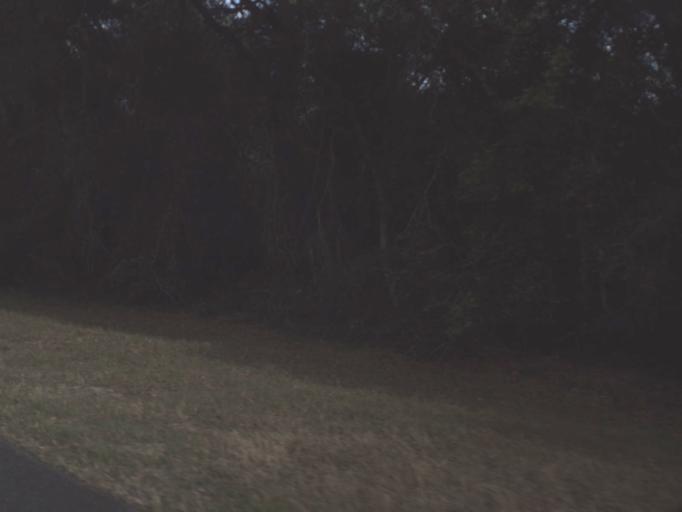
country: US
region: Florida
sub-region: Marion County
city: Silver Springs Shores
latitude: 29.1762
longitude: -81.8358
